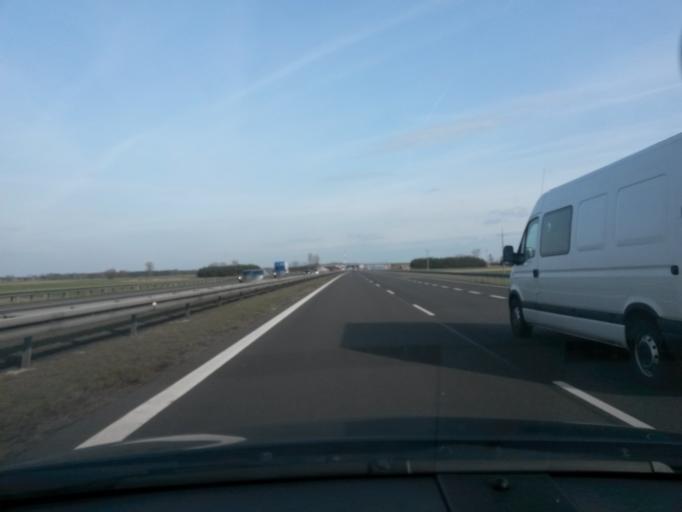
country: PL
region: Greater Poland Voivodeship
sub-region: Powiat slupecki
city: Ladek
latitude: 52.2262
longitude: 17.9333
